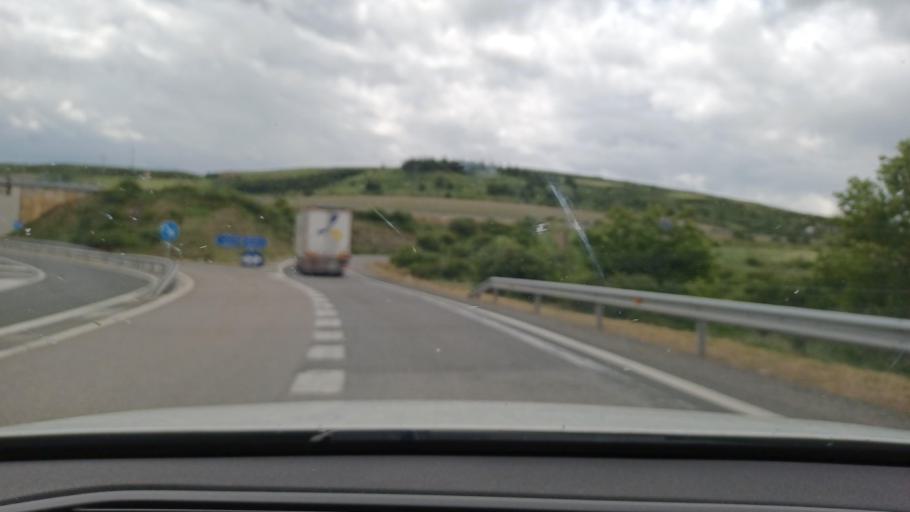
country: ES
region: Castille and Leon
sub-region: Provincia de Burgos
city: Pancorbo
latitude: 42.6247
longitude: -3.1136
